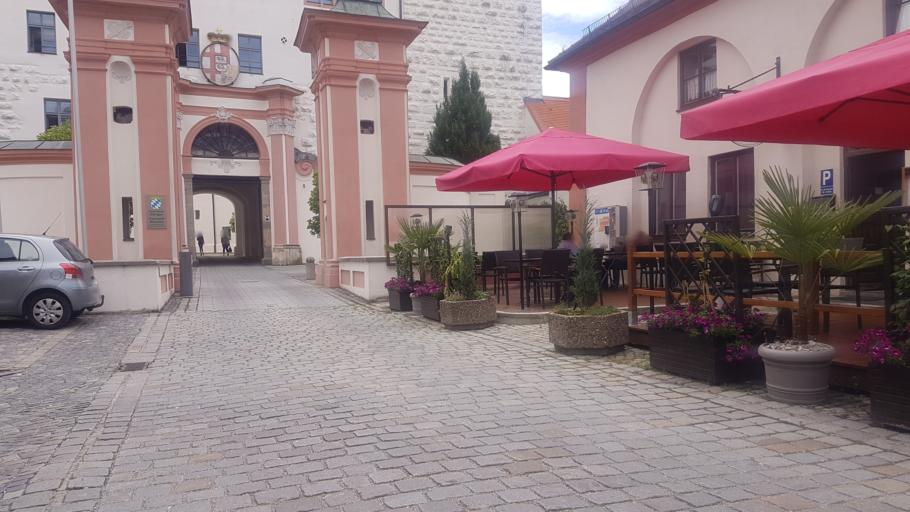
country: DE
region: Bavaria
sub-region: Swabia
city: Dillingen an der Donau
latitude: 48.5768
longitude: 10.4946
